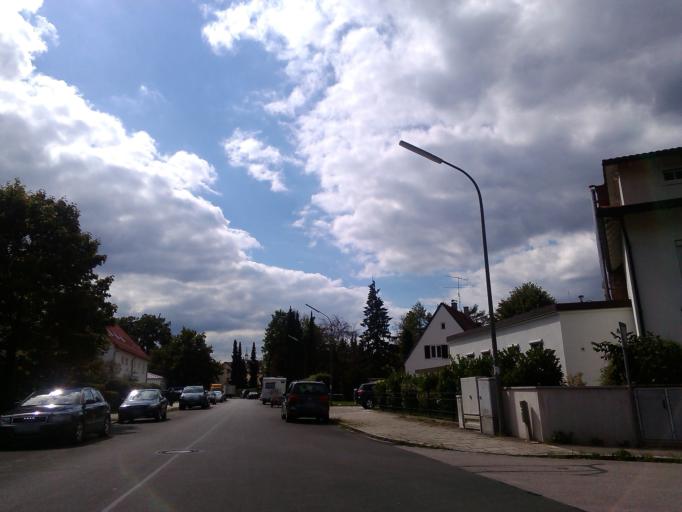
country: DE
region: Bavaria
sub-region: Upper Bavaria
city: Pasing
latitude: 48.1419
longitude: 11.4422
